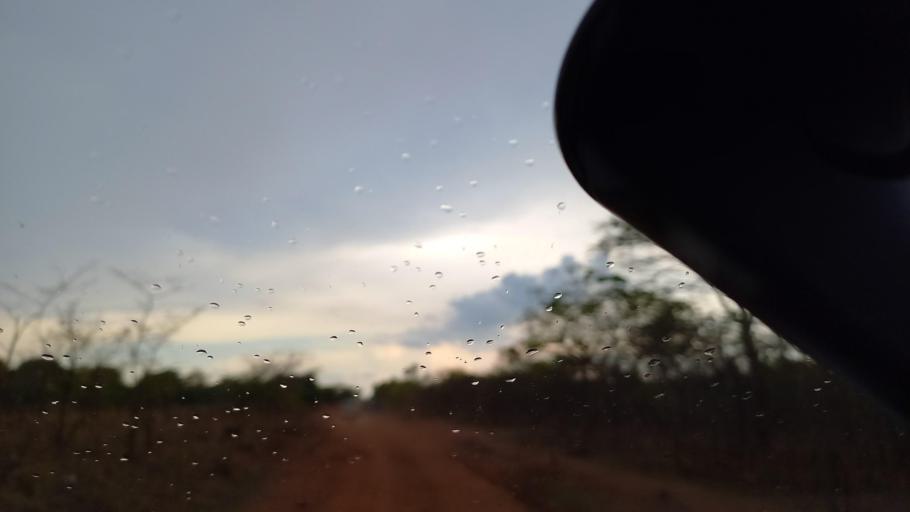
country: ZM
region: Lusaka
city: Kafue
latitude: -15.9833
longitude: 28.2618
